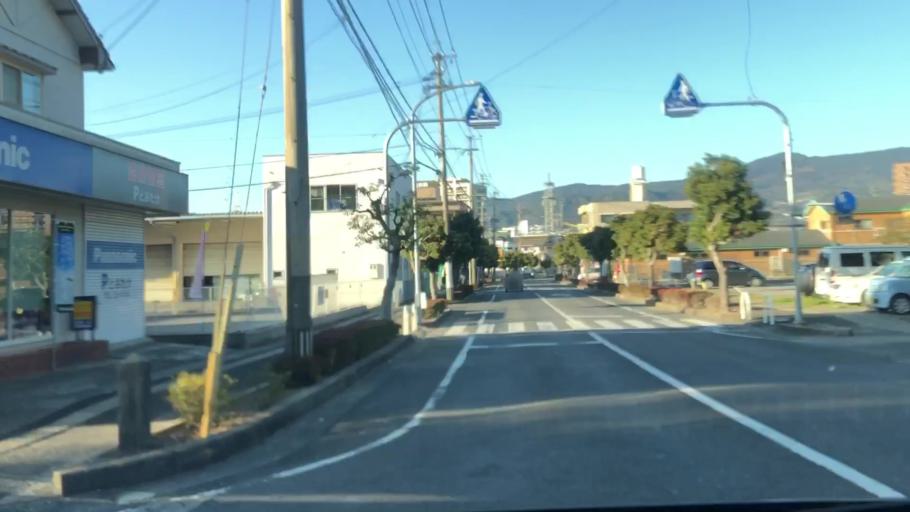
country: JP
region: Nagasaki
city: Sasebo
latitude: 33.1282
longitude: 129.8007
